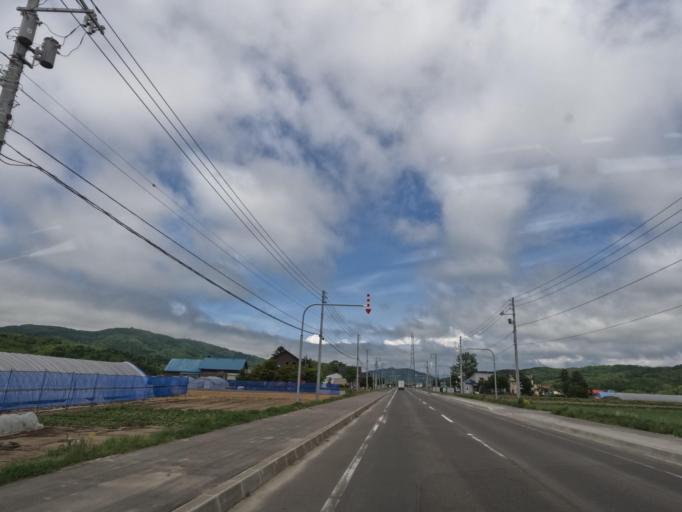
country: JP
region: Hokkaido
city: Tobetsu
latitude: 43.2698
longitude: 141.5294
